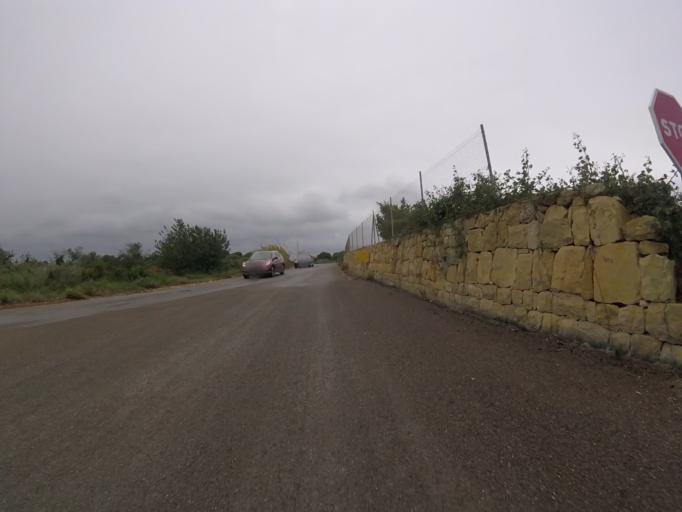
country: ES
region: Valencia
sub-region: Provincia de Castello
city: Alcoceber
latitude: 40.2384
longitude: 0.2506
